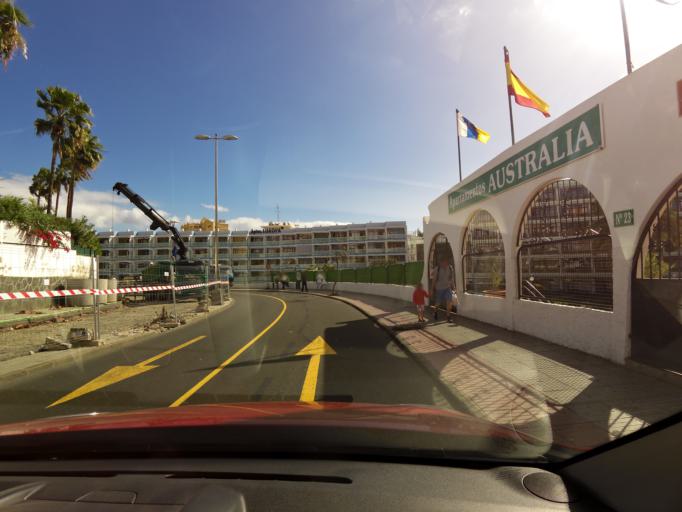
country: ES
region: Canary Islands
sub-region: Provincia de Las Palmas
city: Playa del Ingles
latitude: 27.7586
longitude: -15.5738
